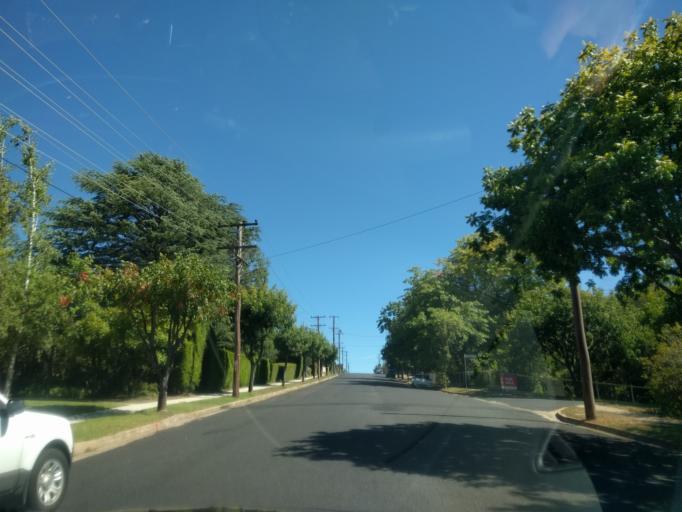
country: AU
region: New South Wales
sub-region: Armidale Dumaresq
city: Armidale
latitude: -30.5215
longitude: 151.6643
